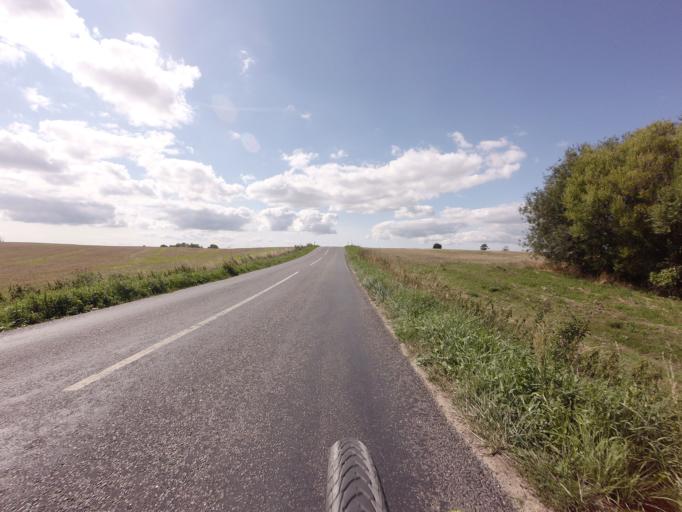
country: DK
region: Zealand
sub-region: Vordingborg Kommune
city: Stege
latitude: 54.9957
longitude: 12.4962
